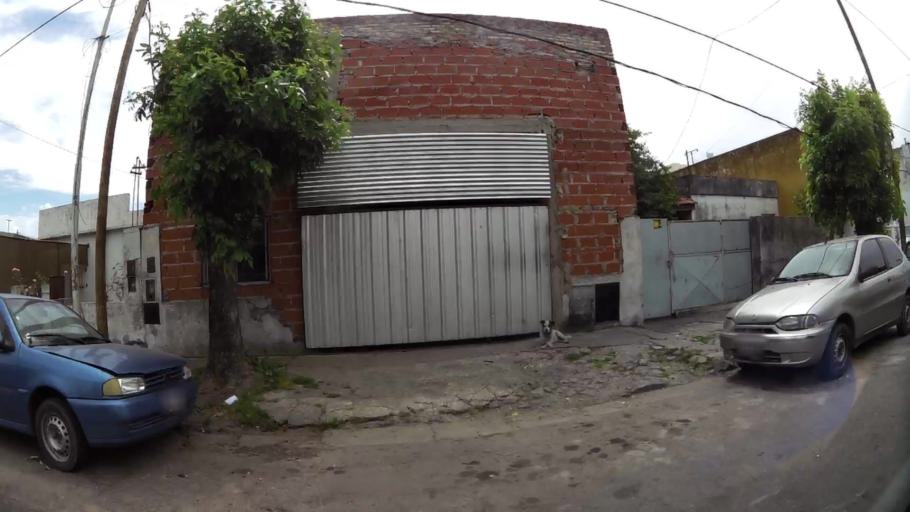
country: AR
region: Buenos Aires
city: San Justo
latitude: -34.6863
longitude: -58.5320
